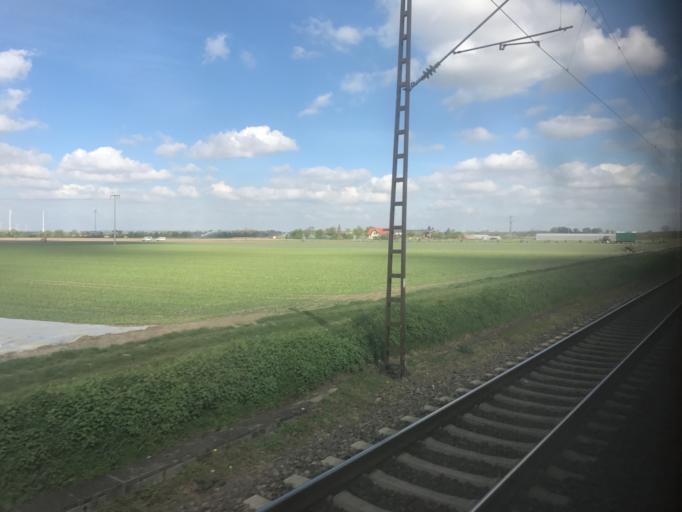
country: DE
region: Rheinland-Pfalz
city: Bobenheim-Roxheim
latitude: 49.5715
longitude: 8.3502
